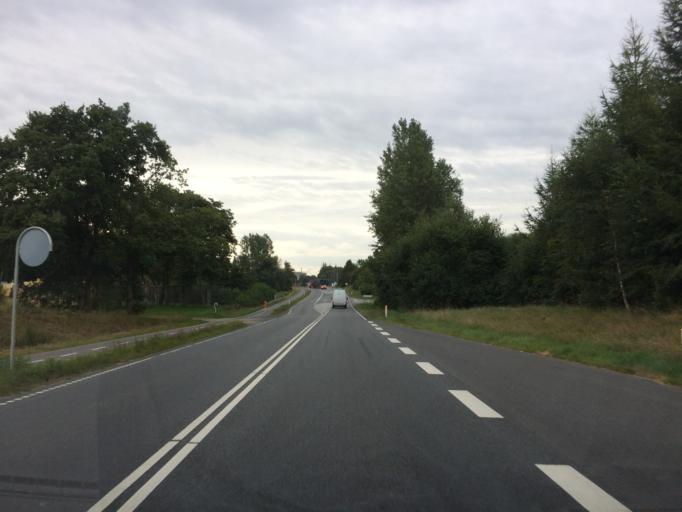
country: DK
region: Central Jutland
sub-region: Ikast-Brande Kommune
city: Brande
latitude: 55.9586
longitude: 9.1059
